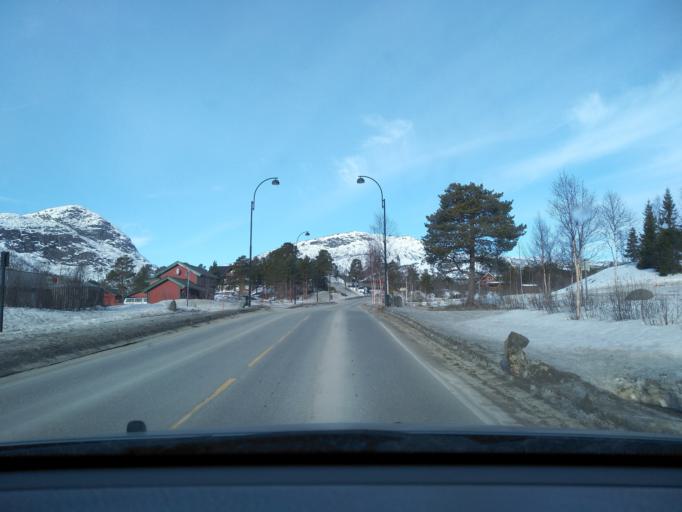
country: NO
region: Aust-Agder
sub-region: Bykle
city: Hovden
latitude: 59.5573
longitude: 7.3590
